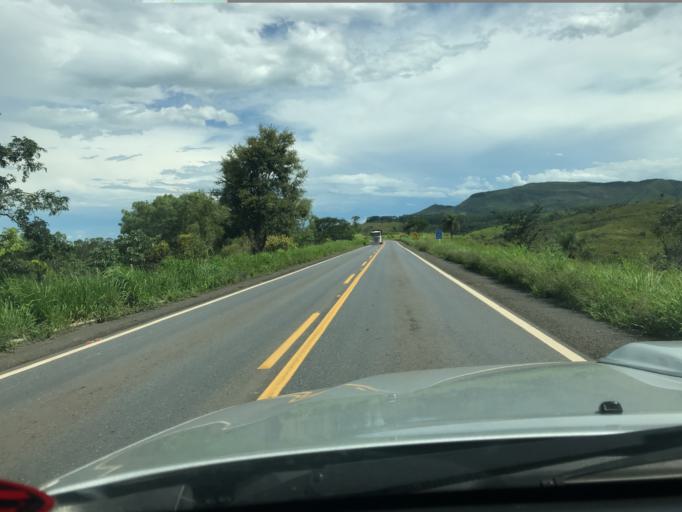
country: BR
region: Minas Gerais
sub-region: Campos Altos
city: Campos Altos
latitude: -19.8006
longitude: -46.0341
